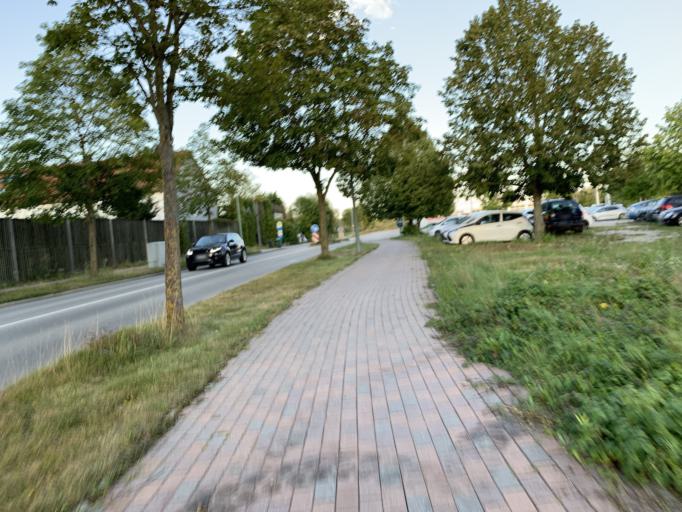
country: DE
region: Bavaria
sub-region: Upper Bavaria
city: Freising
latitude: 48.3836
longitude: 11.7524
